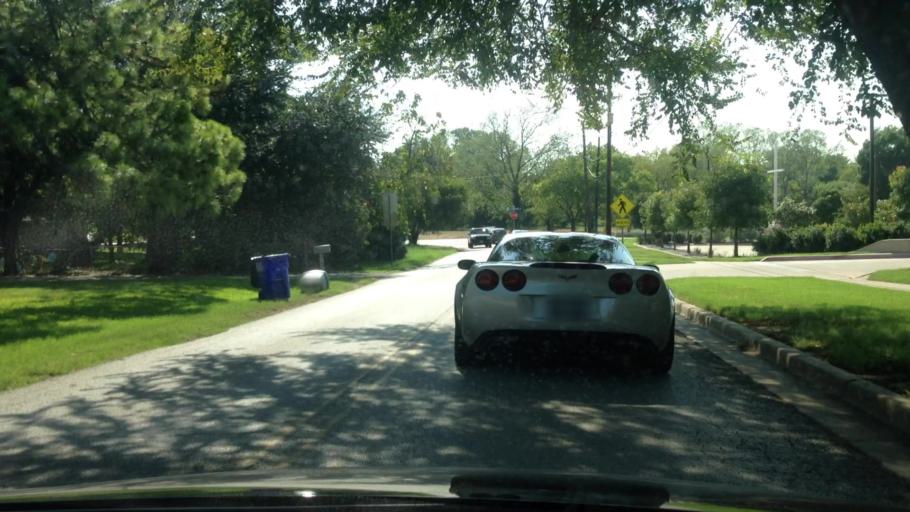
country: US
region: Texas
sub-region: Tarrant County
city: Colleyville
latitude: 32.9004
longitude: -97.1534
